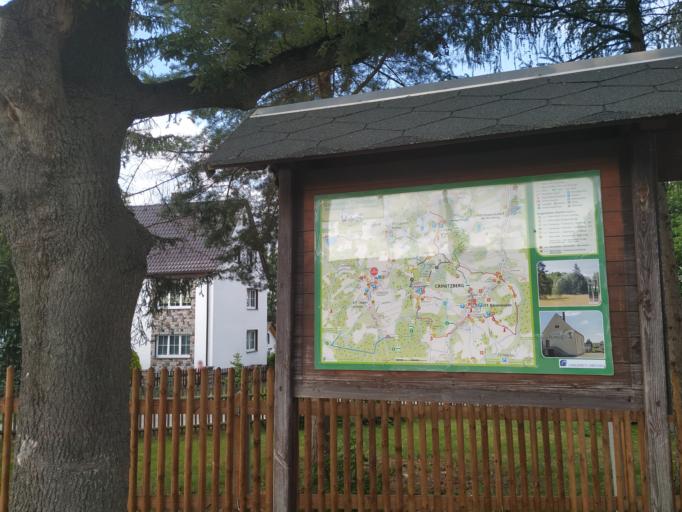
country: DE
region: Saxony
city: Stutzengrun
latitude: 50.5724
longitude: 12.4845
